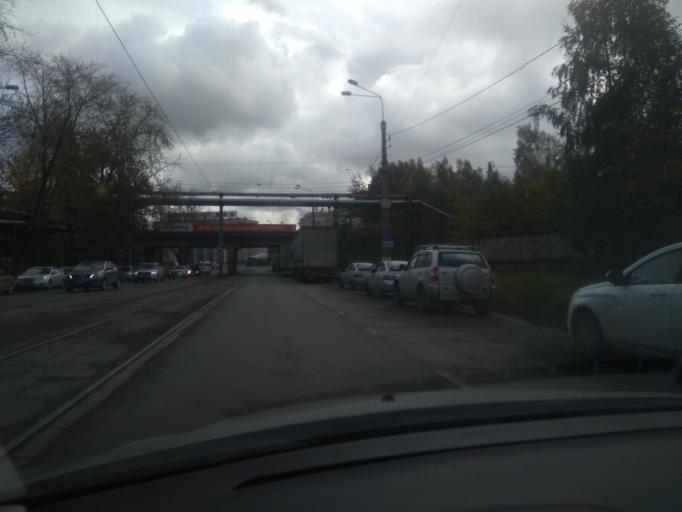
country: RU
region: Sverdlovsk
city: Nizhniy Tagil
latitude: 57.9290
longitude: 60.0077
